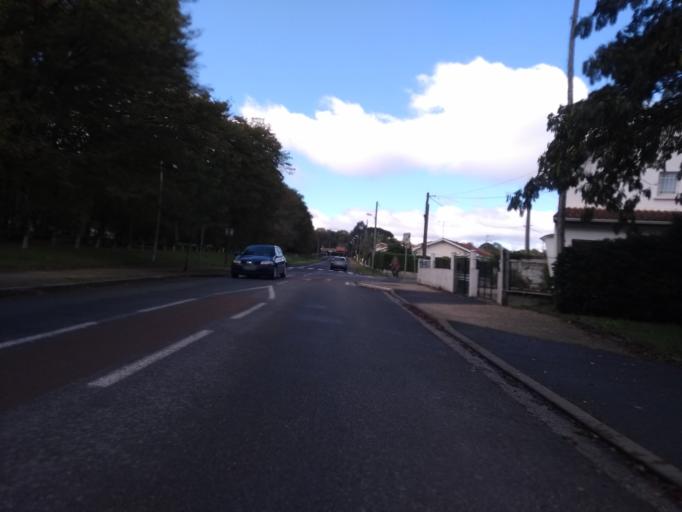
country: FR
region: Aquitaine
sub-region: Departement de la Gironde
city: Gradignan
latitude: 44.7761
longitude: -0.6172
